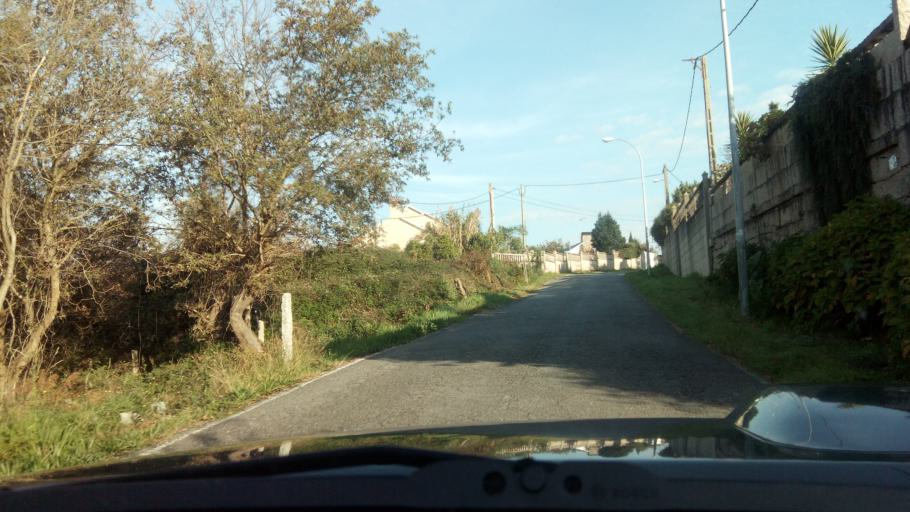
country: ES
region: Galicia
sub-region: Provincia de Pontevedra
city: Marin
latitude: 42.3792
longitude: -8.7262
